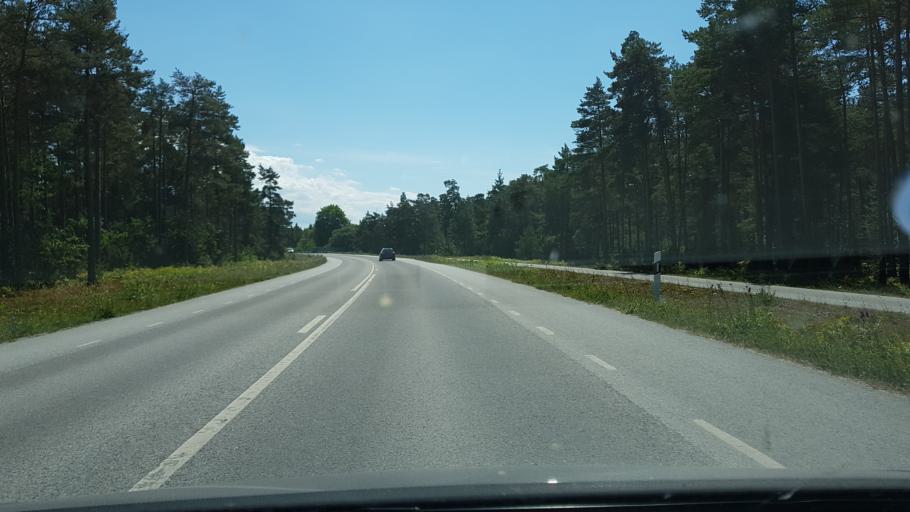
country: SE
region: Gotland
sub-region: Gotland
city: Vibble
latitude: 57.5608
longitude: 18.2028
